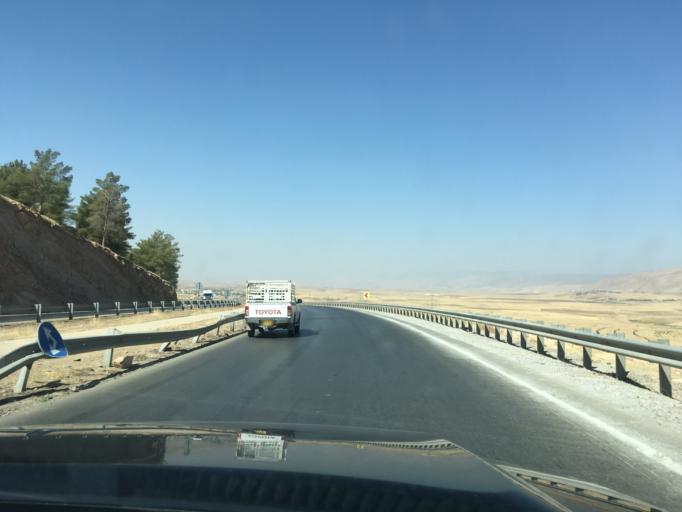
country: IQ
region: Arbil
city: Shaqlawah
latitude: 36.4888
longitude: 44.3796
